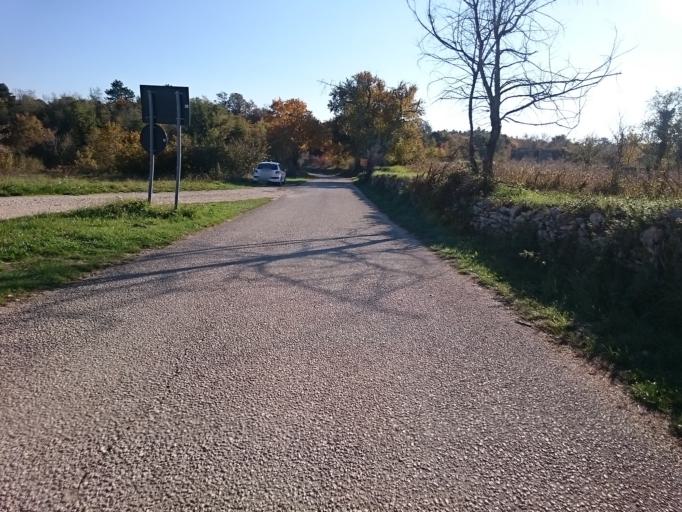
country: HR
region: Istarska
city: Buje
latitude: 45.4031
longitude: 13.7190
